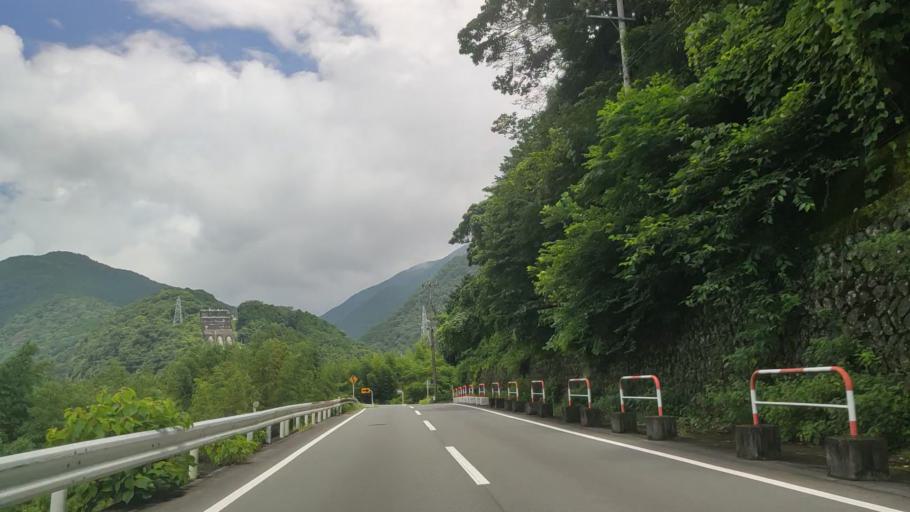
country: JP
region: Shizuoka
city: Fujinomiya
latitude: 35.2347
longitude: 138.5107
